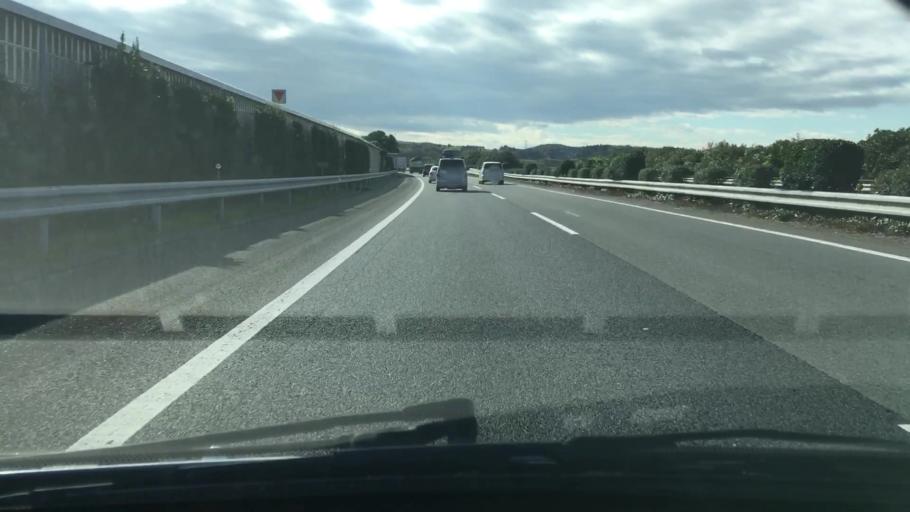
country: JP
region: Chiba
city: Ichihara
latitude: 35.4826
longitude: 140.0818
